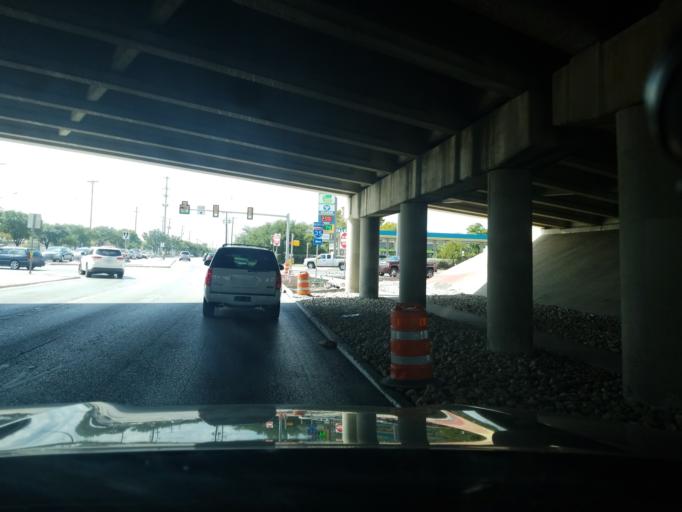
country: US
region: Texas
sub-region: Bexar County
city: San Antonio
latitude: 29.3505
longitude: -98.5344
